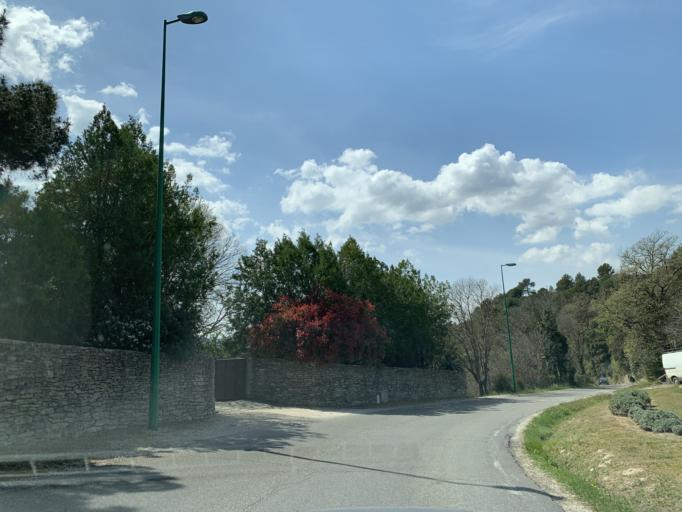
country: FR
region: Provence-Alpes-Cote d'Azur
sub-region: Departement du Vaucluse
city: Goult
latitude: 43.8600
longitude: 5.2401
